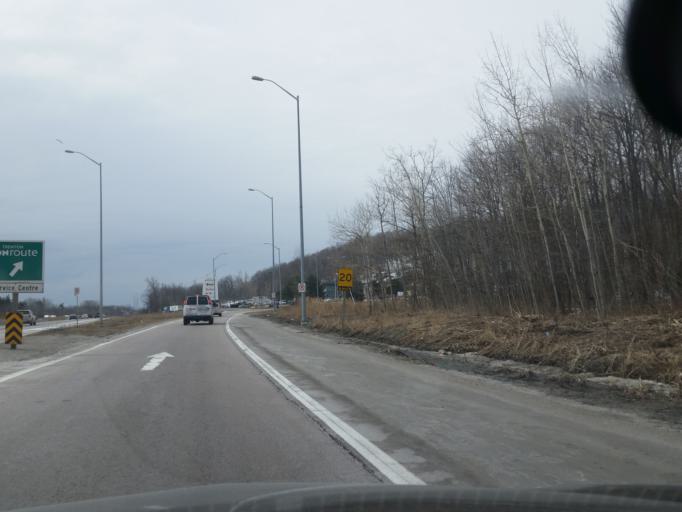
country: CA
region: Ontario
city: Quinte West
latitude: 44.1120
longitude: -77.6559
